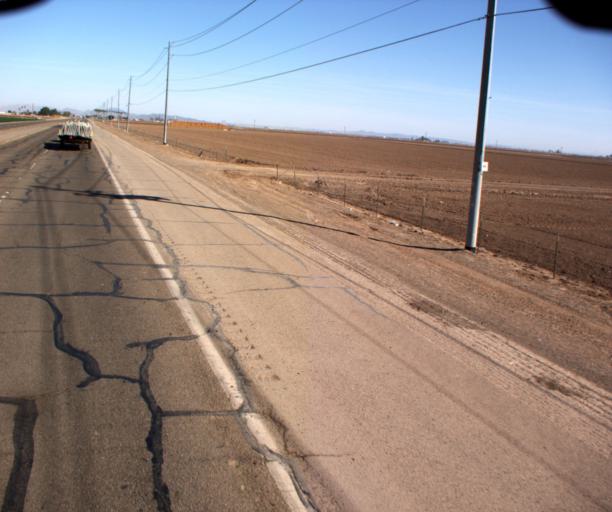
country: US
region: Arizona
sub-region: Yuma County
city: Somerton
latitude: 32.5778
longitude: -114.7698
